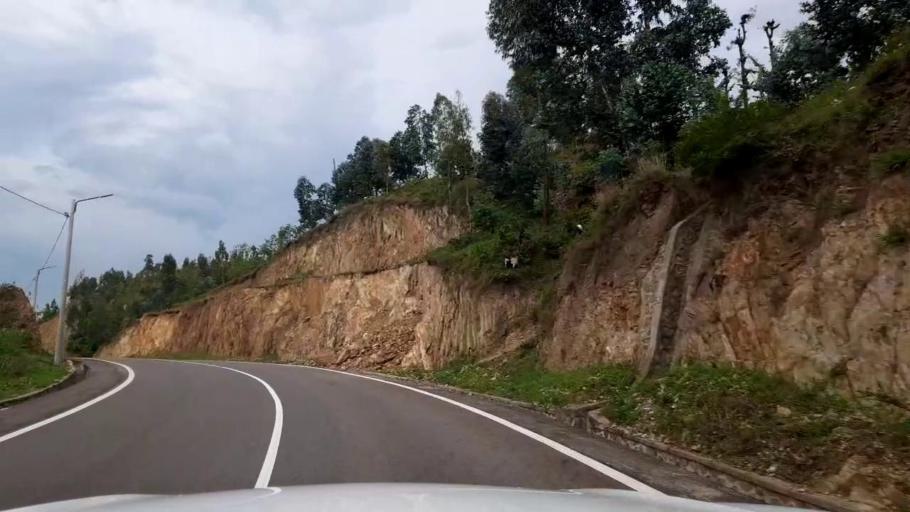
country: RW
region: Western Province
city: Kibuye
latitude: -2.0267
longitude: 29.3927
